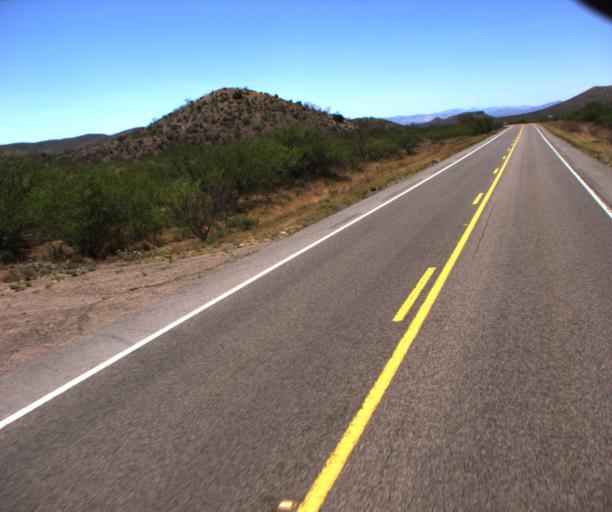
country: US
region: Arizona
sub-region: Cochise County
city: Douglas
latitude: 31.4803
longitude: -109.4450
